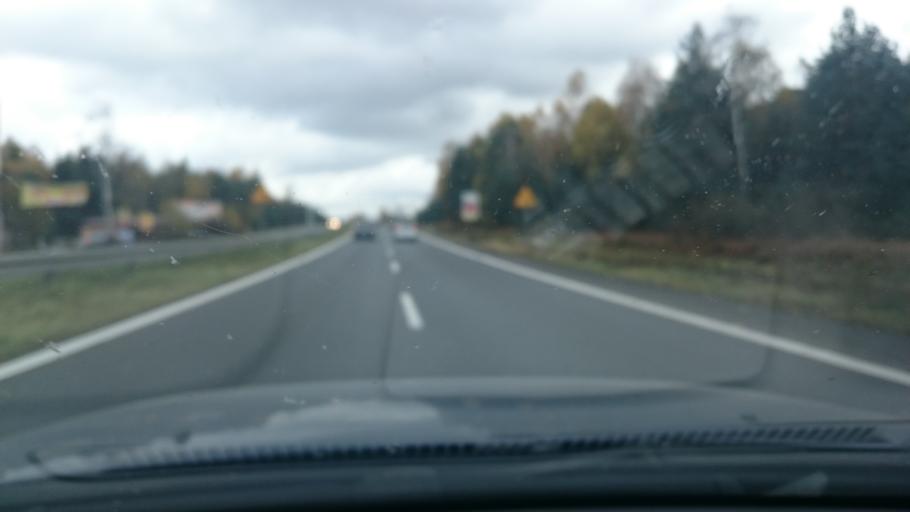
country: PL
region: Lesser Poland Voivodeship
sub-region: Powiat olkuski
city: Boleslaw
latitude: 50.2884
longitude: 19.5176
